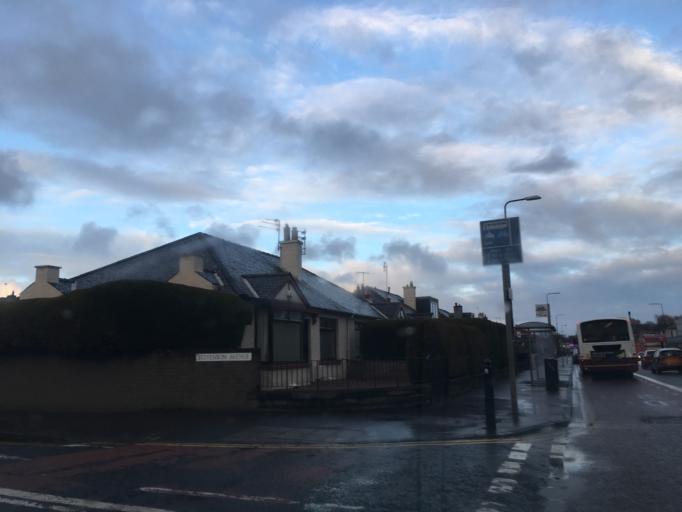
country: GB
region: Scotland
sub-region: Edinburgh
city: Colinton
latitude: 55.9357
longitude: -3.2459
